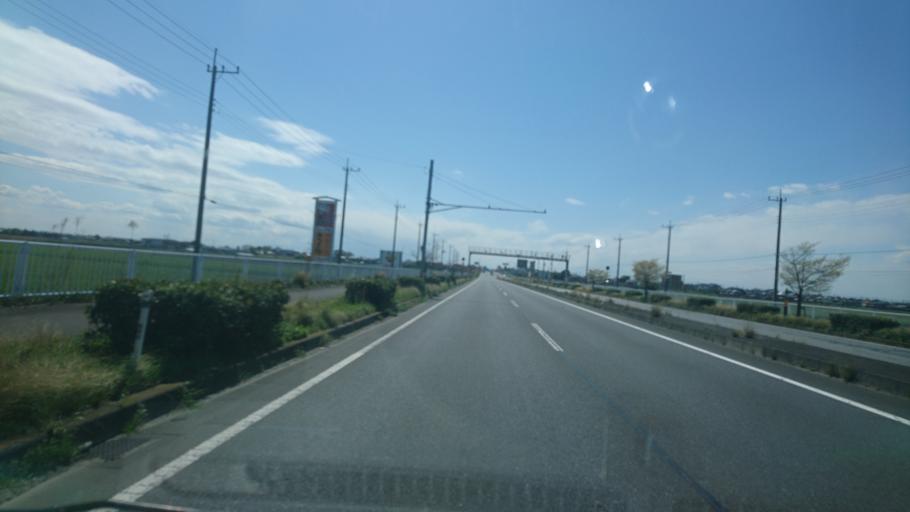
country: JP
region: Ibaraki
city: Yuki
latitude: 36.2910
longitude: 139.8922
